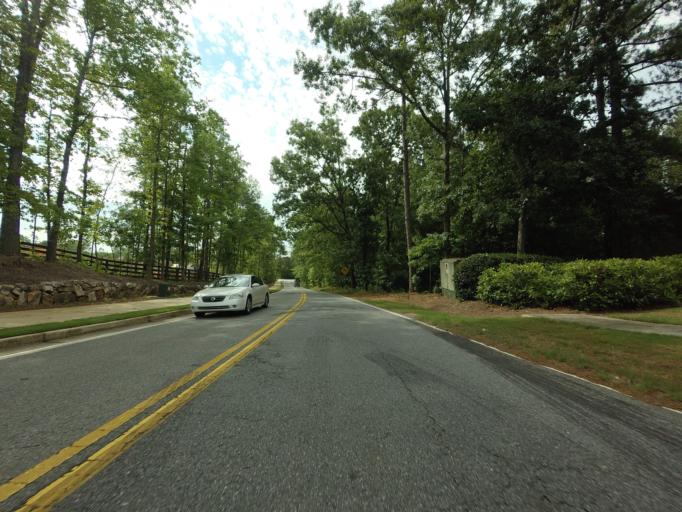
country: US
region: Georgia
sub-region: Gwinnett County
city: Duluth
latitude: 34.0496
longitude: -84.1440
